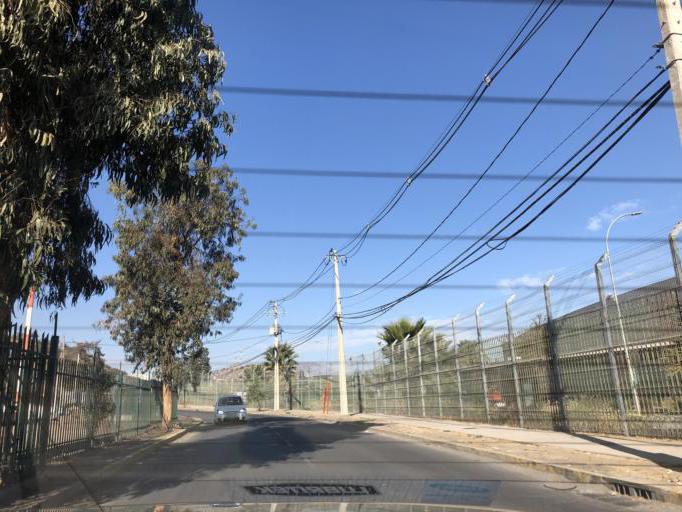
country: CL
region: Santiago Metropolitan
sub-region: Provincia de Cordillera
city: Puente Alto
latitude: -33.6161
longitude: -70.6034
